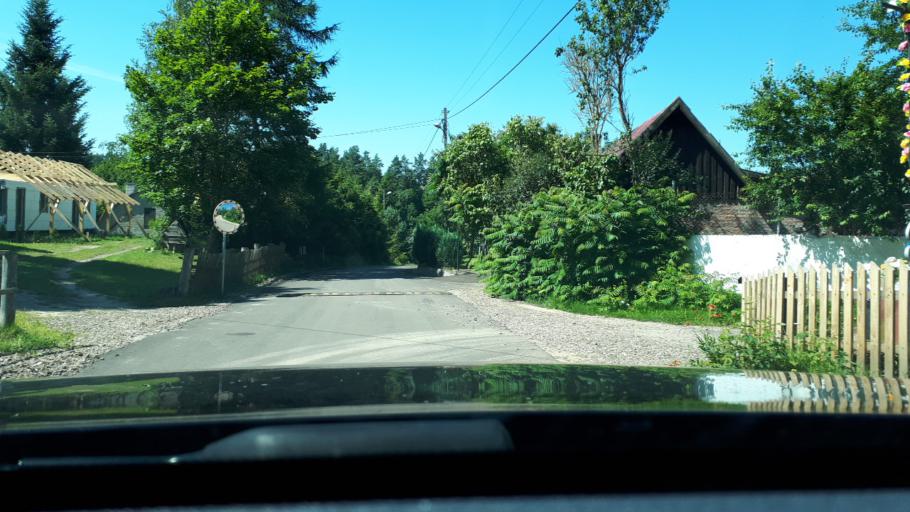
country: PL
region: Warmian-Masurian Voivodeship
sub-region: Powiat olsztynski
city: Gietrzwald
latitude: 53.6904
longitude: 20.2182
